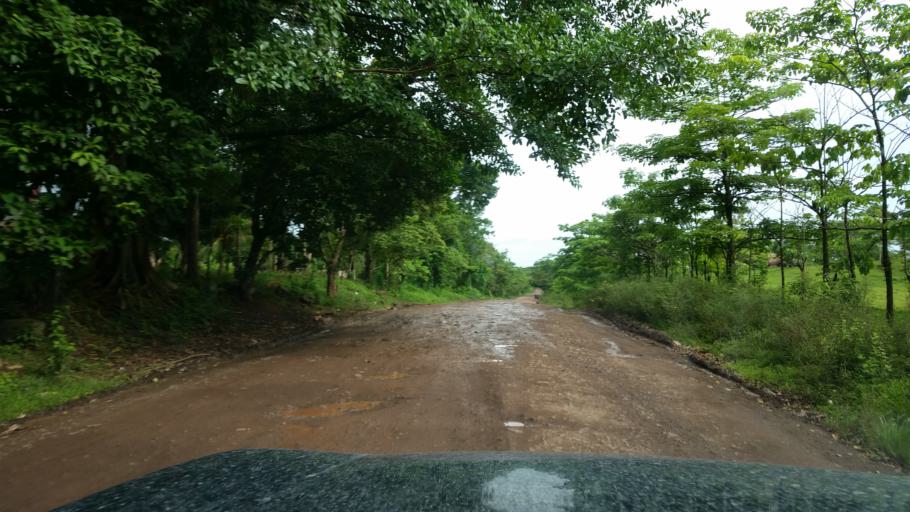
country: NI
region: Atlantico Norte (RAAN)
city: Siuna
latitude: 13.4214
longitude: -84.8531
